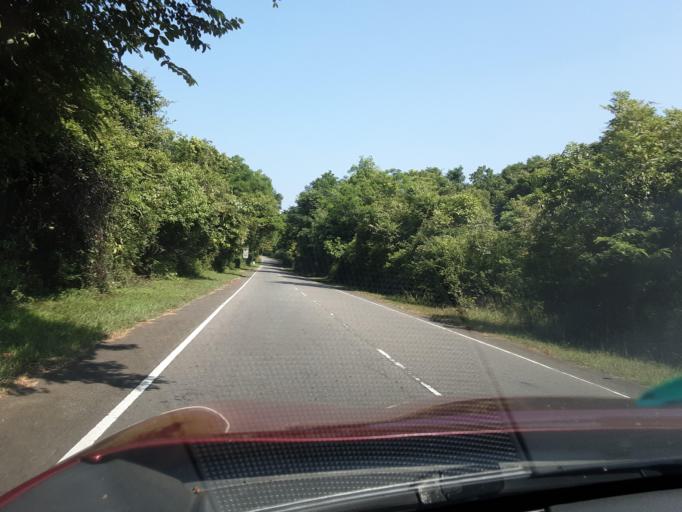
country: LK
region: Uva
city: Badulla
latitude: 7.2673
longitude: 81.0519
